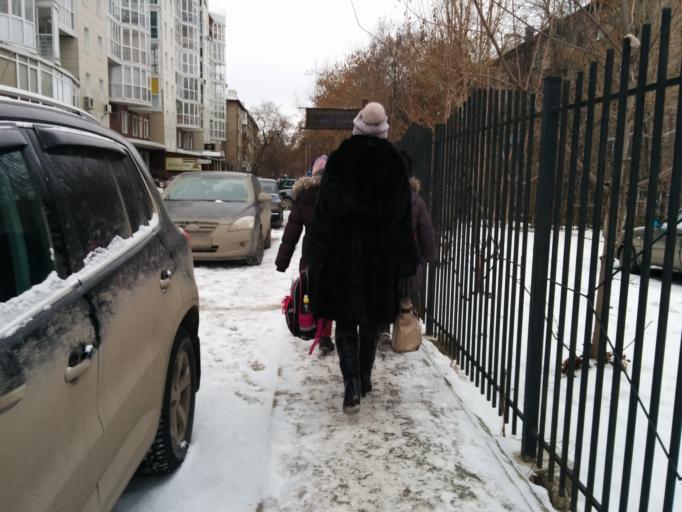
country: RU
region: Perm
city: Perm
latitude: 58.0061
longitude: 56.2169
